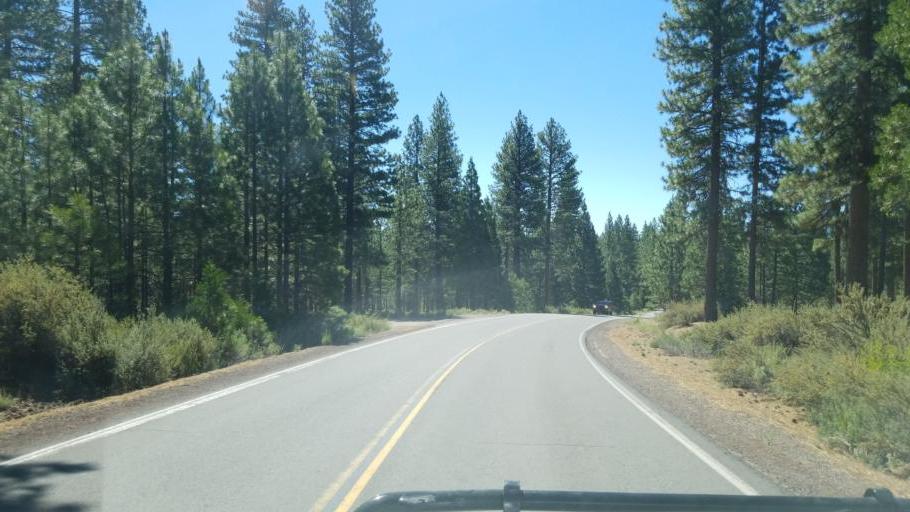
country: US
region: California
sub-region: Lassen County
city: Susanville
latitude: 40.4324
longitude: -120.7318
